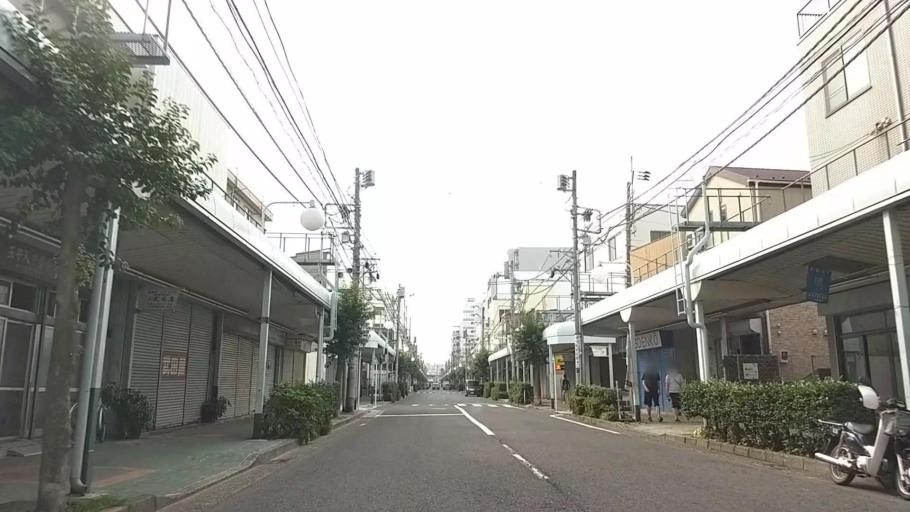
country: JP
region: Kanagawa
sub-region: Kawasaki-shi
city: Kawasaki
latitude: 35.5033
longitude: 139.6808
